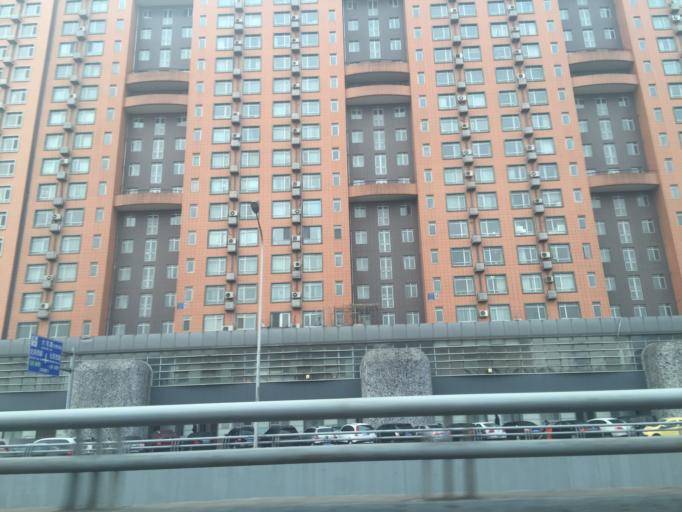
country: CN
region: Beijing
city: Datun
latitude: 40.0007
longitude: 116.3789
